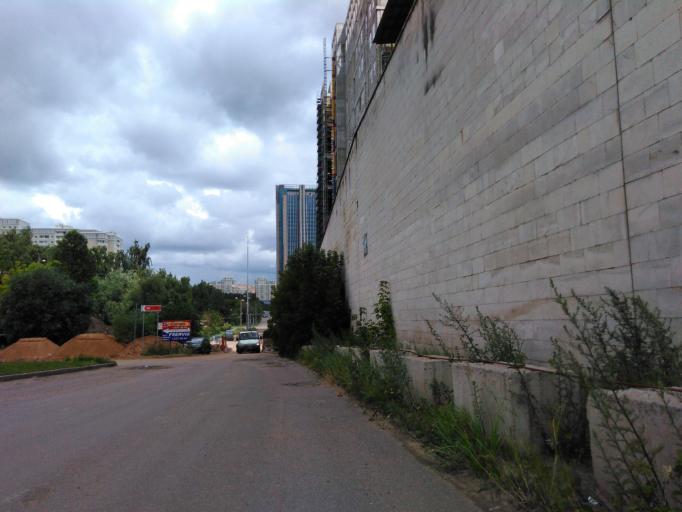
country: RU
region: Moscow
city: Ramenki
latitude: 55.6846
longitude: 37.5173
